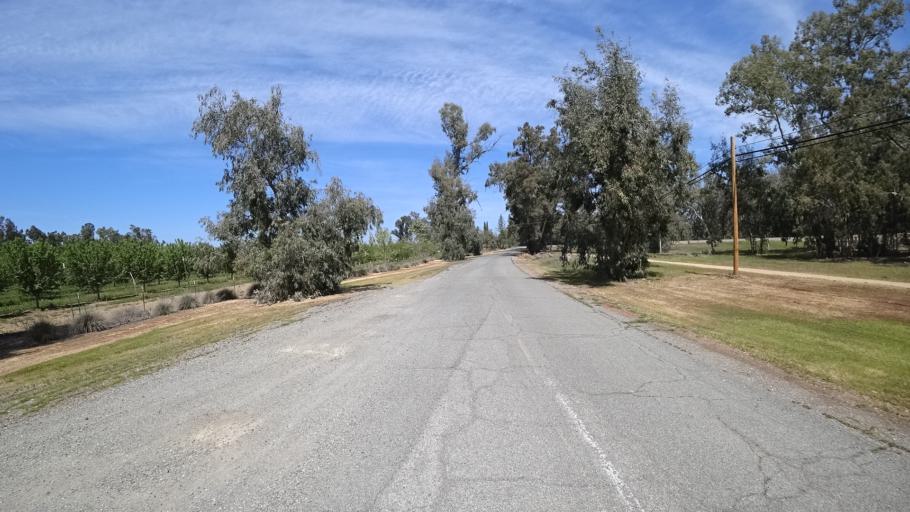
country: US
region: California
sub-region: Glenn County
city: Willows
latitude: 39.5880
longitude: -122.1956
